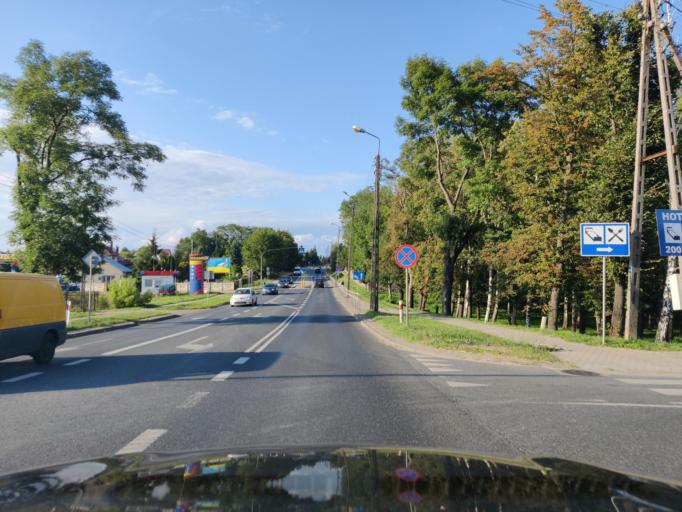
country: PL
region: Masovian Voivodeship
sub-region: Powiat pultuski
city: Pultusk
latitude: 52.7160
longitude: 21.0844
